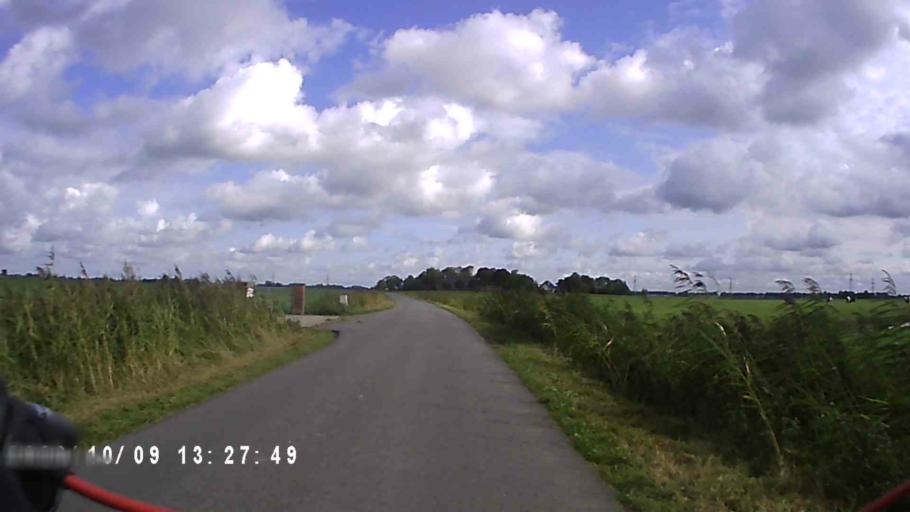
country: NL
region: Groningen
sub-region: Gemeente Zuidhorn
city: Aduard
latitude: 53.2689
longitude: 6.4614
